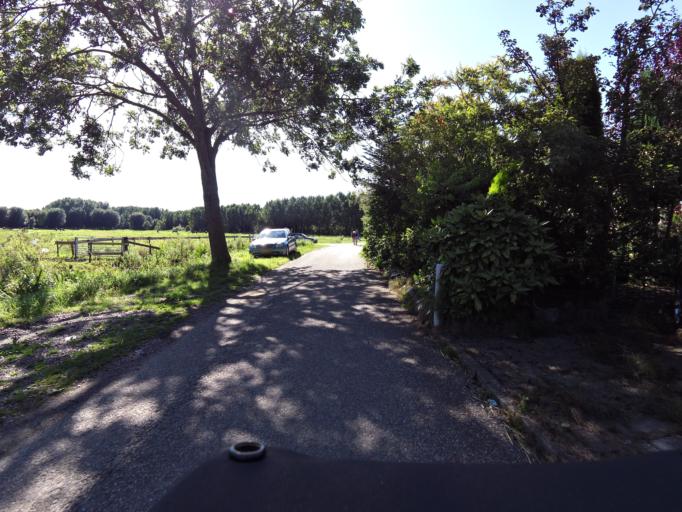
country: NL
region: South Holland
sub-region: Gemeente Spijkenisse
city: Spijkenisse
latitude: 51.8472
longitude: 4.3081
